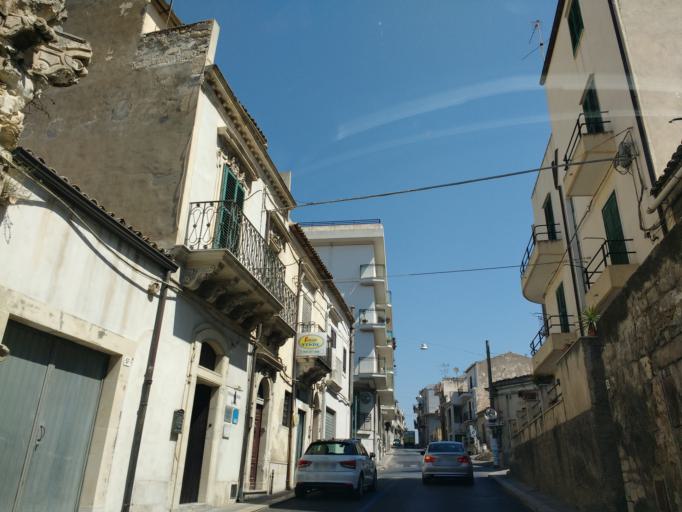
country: IT
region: Sicily
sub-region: Ragusa
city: Scicli
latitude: 36.7956
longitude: 14.7072
